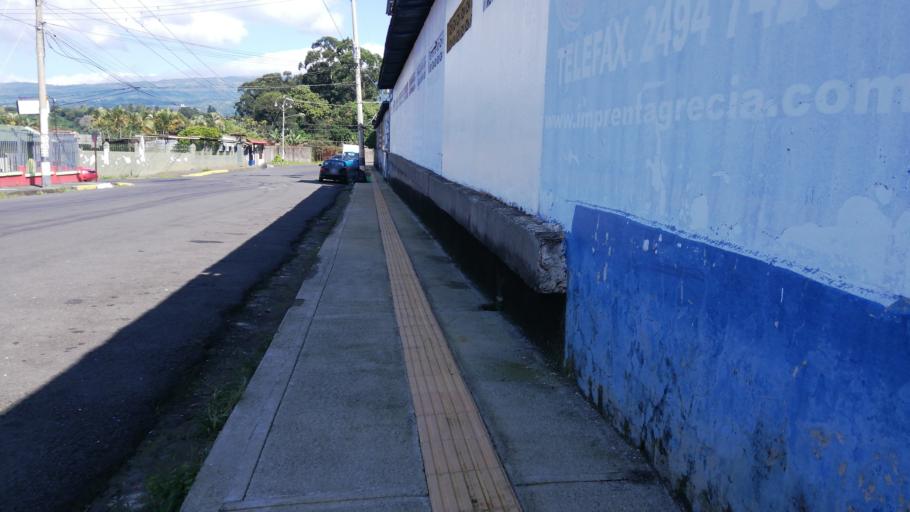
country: CR
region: Alajuela
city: San Juan
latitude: 10.0758
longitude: -84.3103
